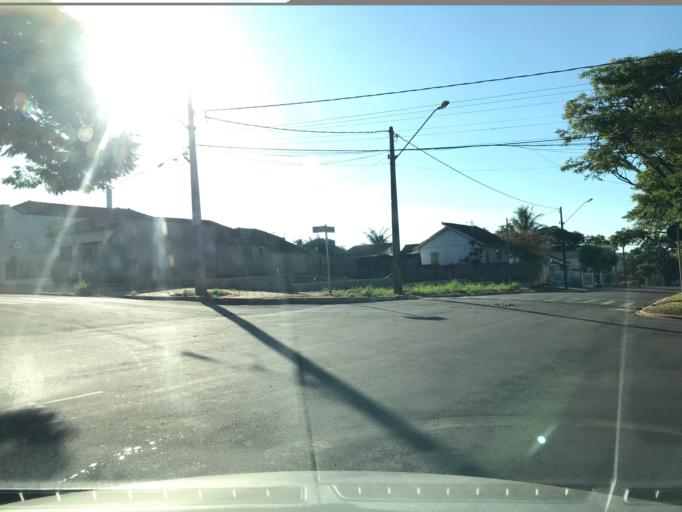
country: BR
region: Parana
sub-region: Ipora
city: Ipora
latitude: -24.0027
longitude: -53.7163
